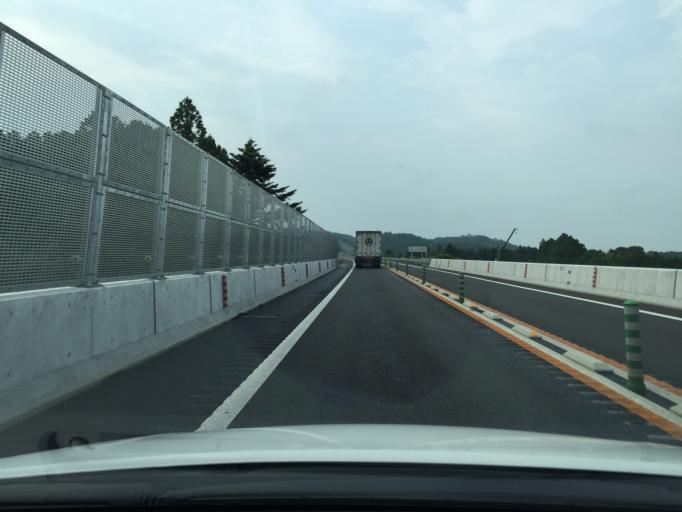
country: JP
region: Fukushima
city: Namie
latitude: 37.4265
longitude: 140.9616
